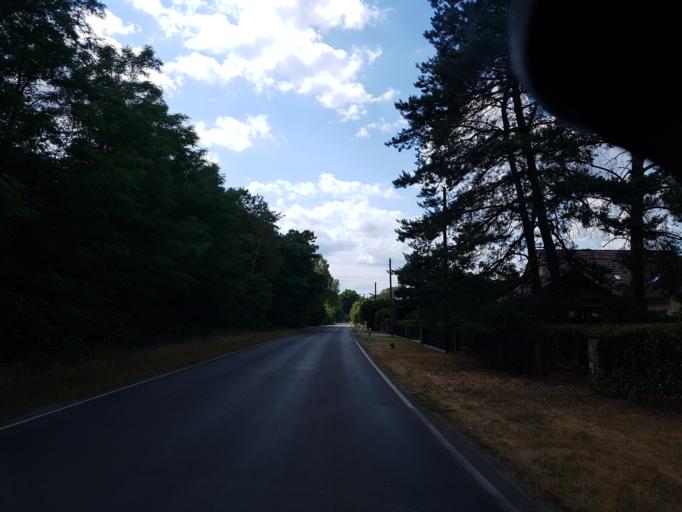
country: DE
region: Brandenburg
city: Cottbus
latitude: 51.7203
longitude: 14.3817
